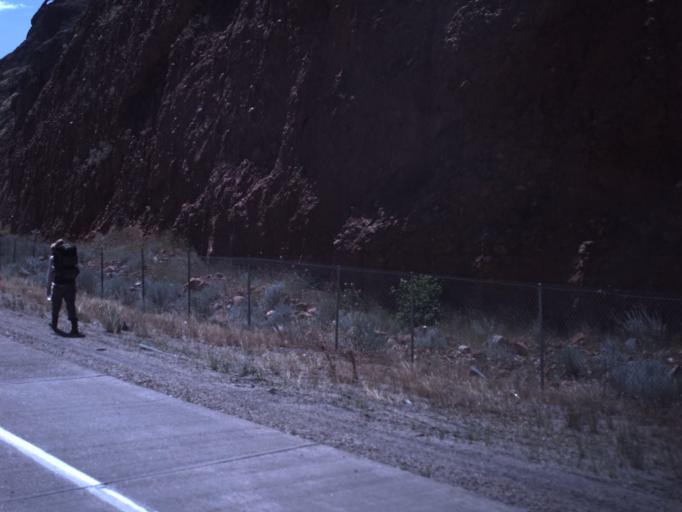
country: US
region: Utah
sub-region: Morgan County
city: Morgan
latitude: 41.0555
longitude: -111.5312
